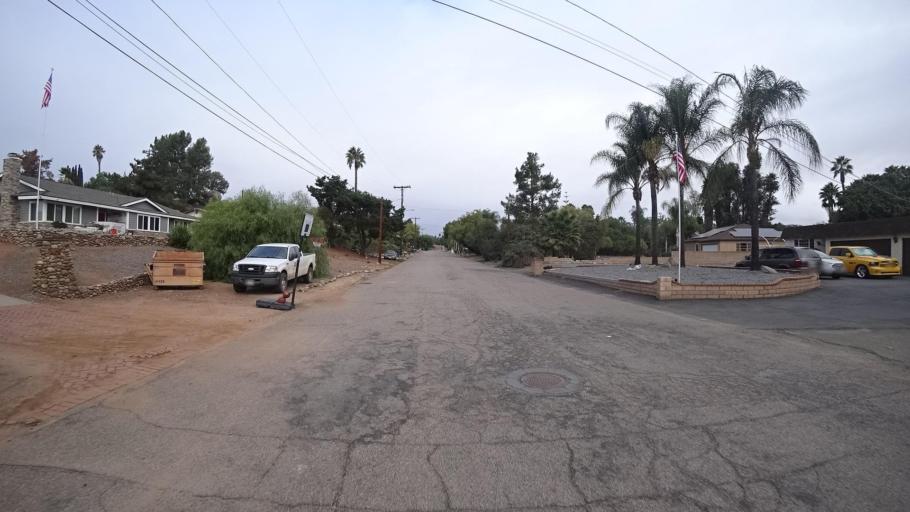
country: US
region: California
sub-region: San Diego County
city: Rancho San Diego
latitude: 32.7593
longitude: -116.9257
